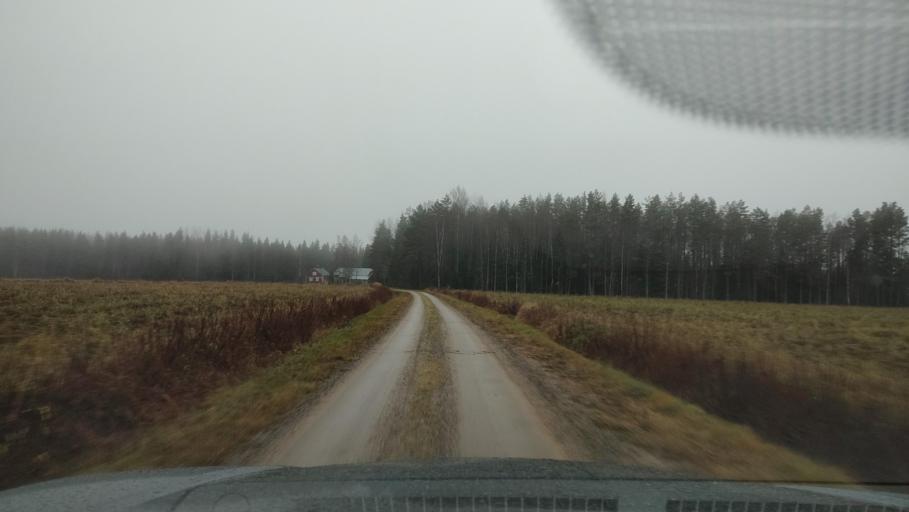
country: FI
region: Southern Ostrobothnia
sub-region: Suupohja
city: Karijoki
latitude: 62.1886
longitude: 21.7717
